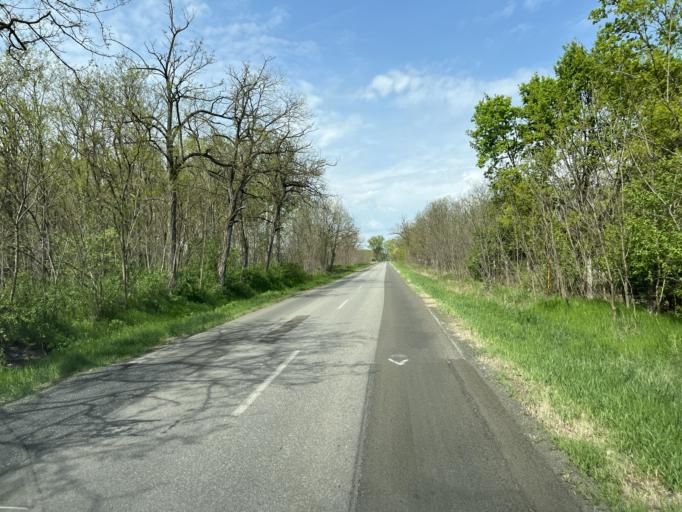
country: HU
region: Pest
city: Albertirsa
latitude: 47.1957
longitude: 19.6119
